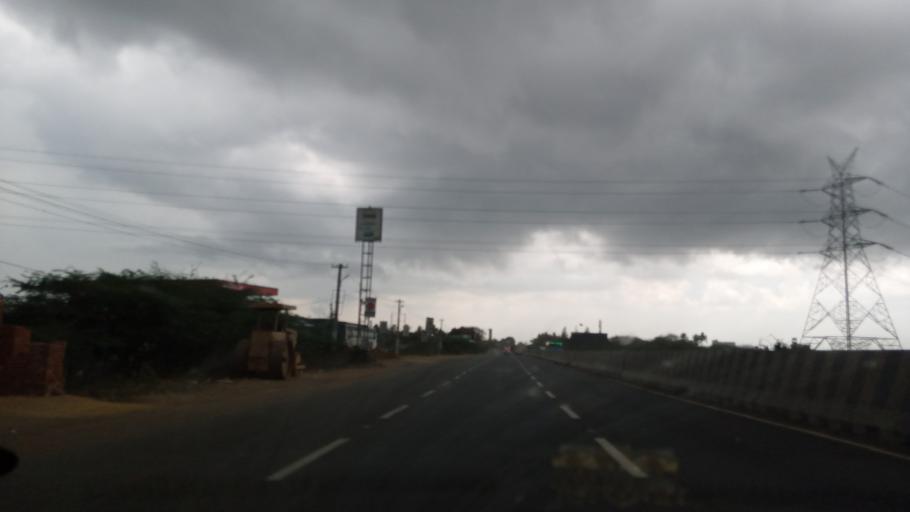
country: IN
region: Tamil Nadu
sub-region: Kancheepuram
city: Madambakkam
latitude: 12.8744
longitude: 79.9938
